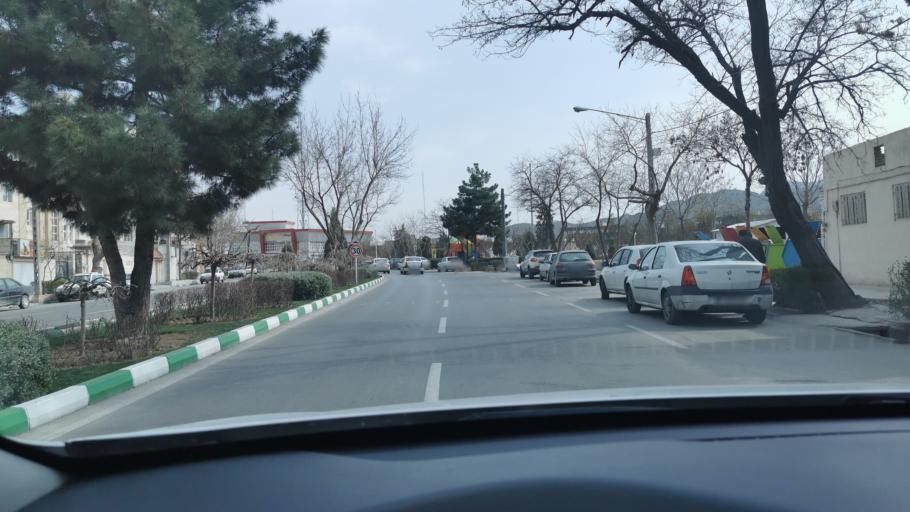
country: IR
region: Razavi Khorasan
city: Mashhad
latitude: 36.2751
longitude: 59.5670
